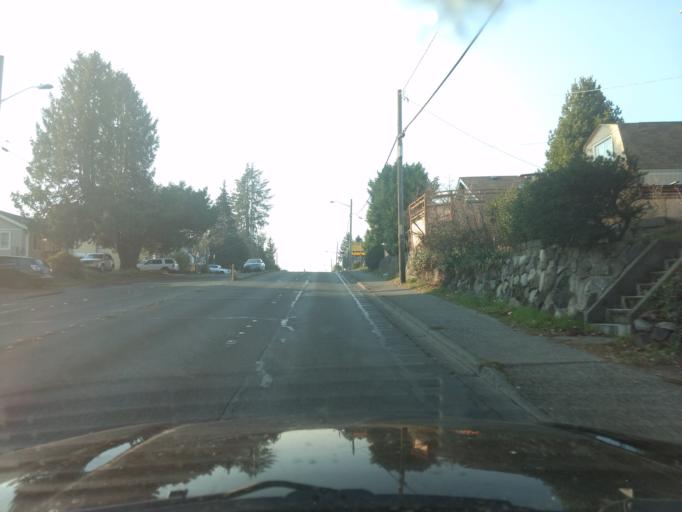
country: US
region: Washington
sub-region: Kitsap County
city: Bremerton
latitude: 47.5710
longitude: -122.6359
